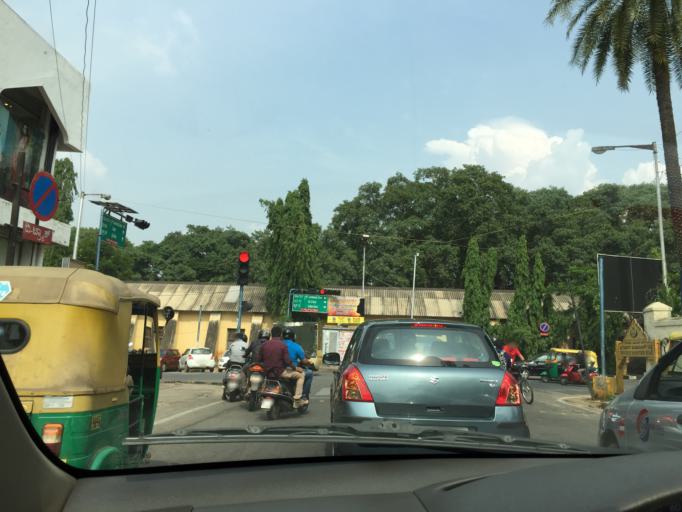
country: IN
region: Karnataka
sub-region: Bangalore Urban
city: Bangalore
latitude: 12.9794
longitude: 77.6068
